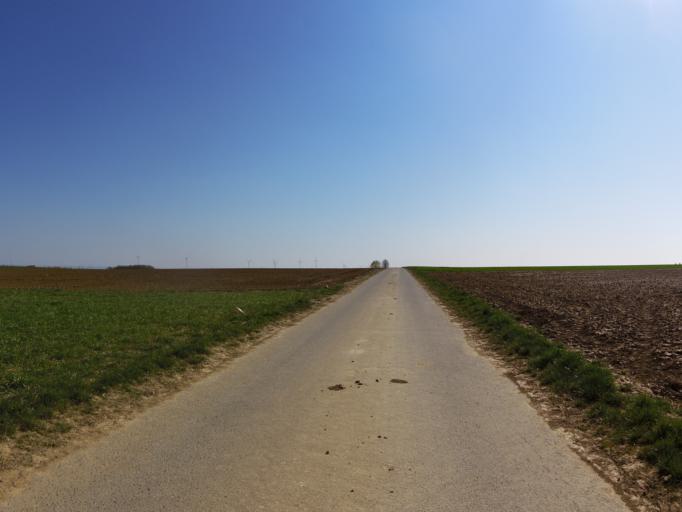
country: DE
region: Bavaria
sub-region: Regierungsbezirk Unterfranken
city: Biebelried
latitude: 49.8161
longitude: 10.0934
